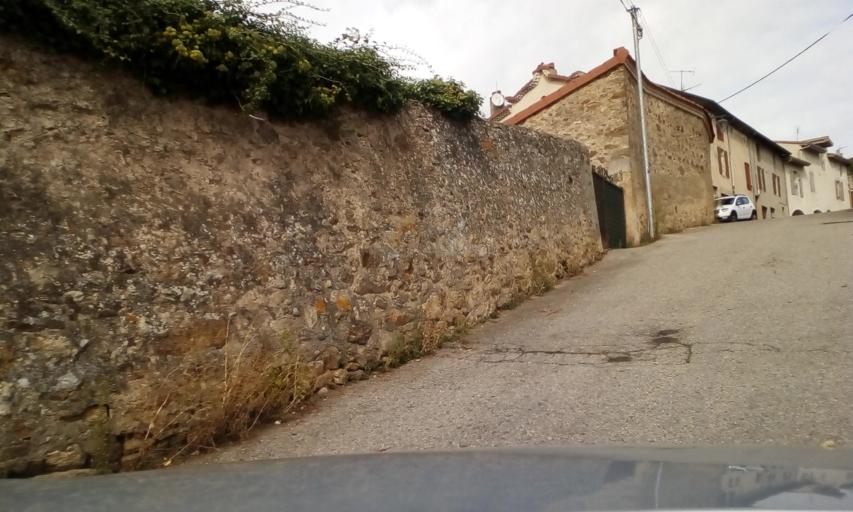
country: FR
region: Rhone-Alpes
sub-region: Departement de l'Ardeche
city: Boulieu-les-Annonay
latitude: 45.2691
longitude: 4.6645
